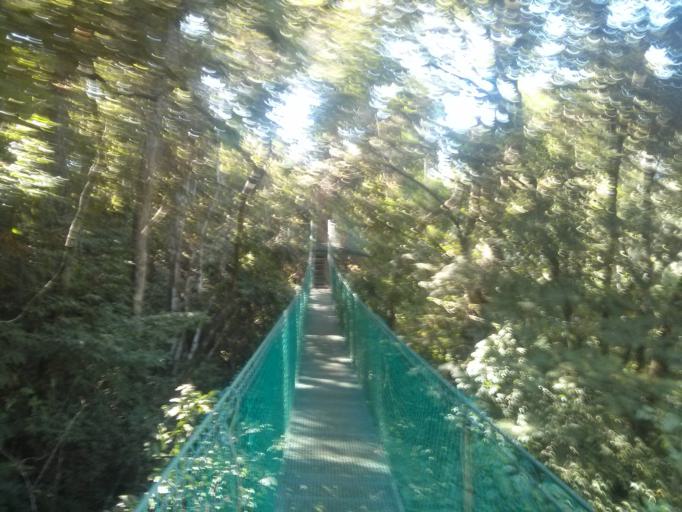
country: CR
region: Puntarenas
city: Paquera
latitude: 9.6538
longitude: -85.0770
